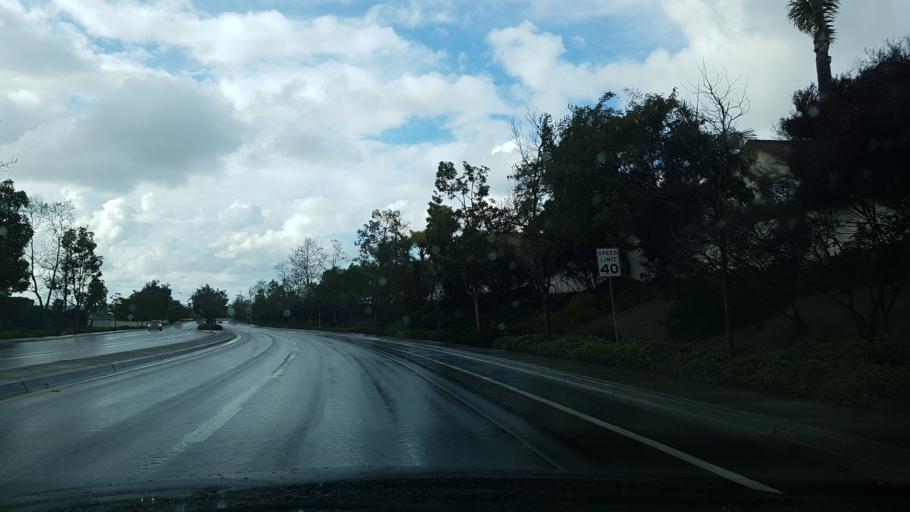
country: US
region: California
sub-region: San Diego County
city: Fairbanks Ranch
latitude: 32.9305
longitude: -117.1979
